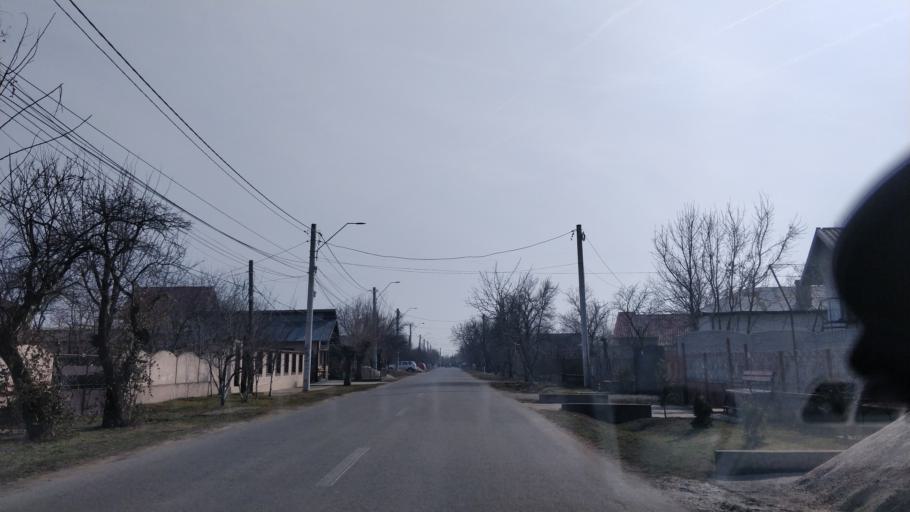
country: RO
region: Giurgiu
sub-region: Comuna Bolintin Vale
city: Bolintin Vale
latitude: 44.4626
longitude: 25.7777
